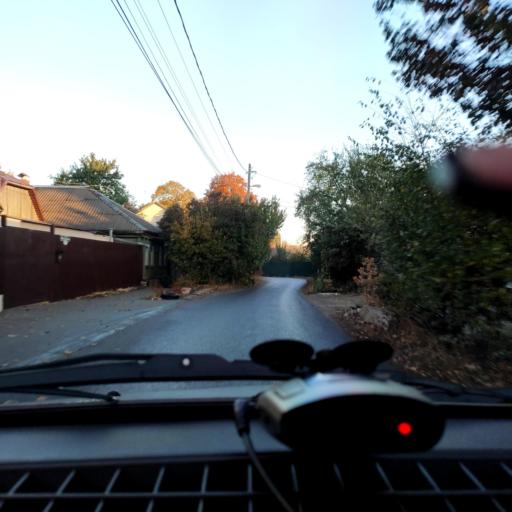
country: RU
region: Voronezj
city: Voronezh
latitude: 51.6854
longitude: 39.2079
